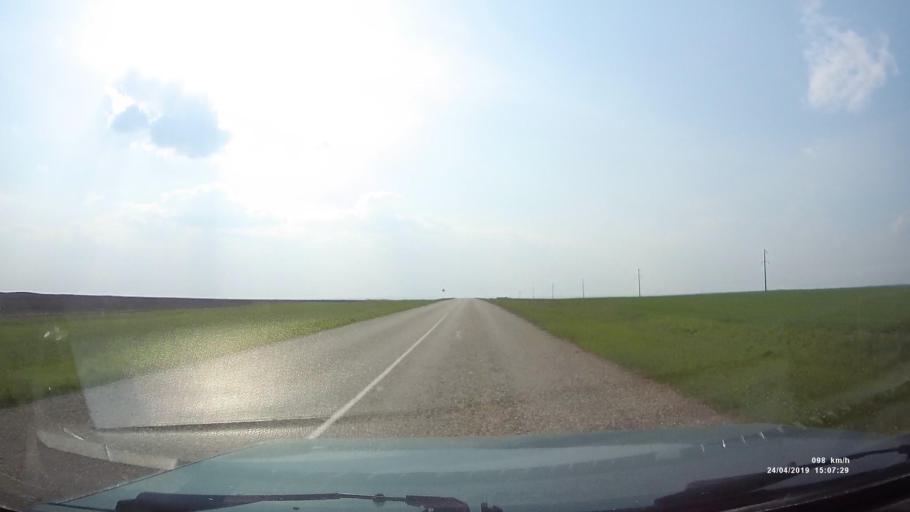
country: RU
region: Rostov
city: Remontnoye
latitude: 46.5597
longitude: 43.4041
